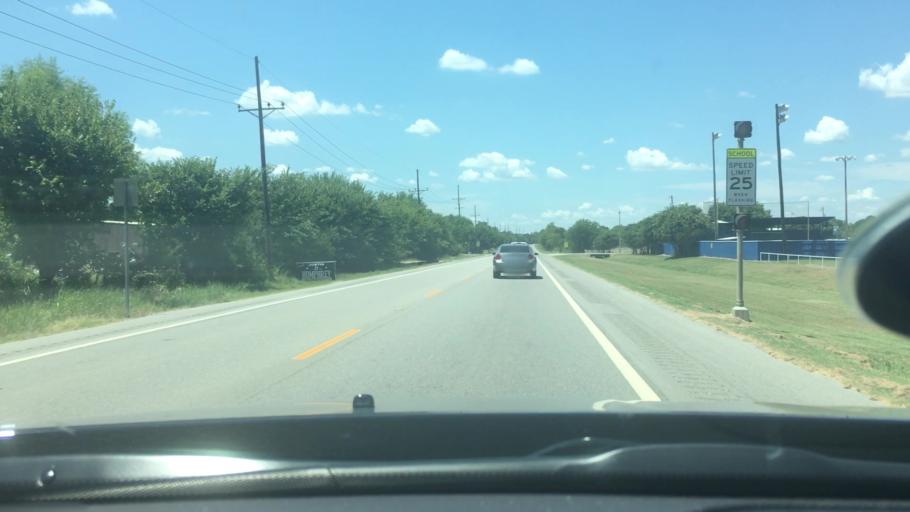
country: US
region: Oklahoma
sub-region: Bryan County
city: Durant
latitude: 33.9984
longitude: -96.2260
